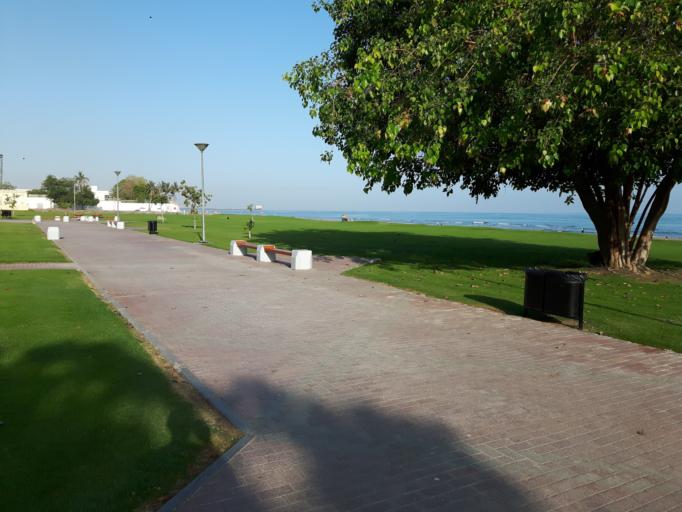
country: OM
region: Muhafazat Masqat
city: Bawshar
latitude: 23.6089
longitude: 58.4414
